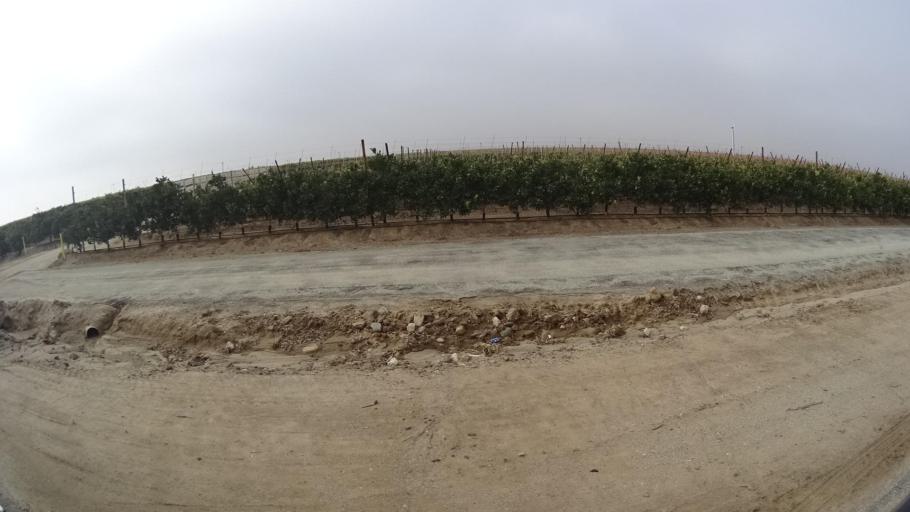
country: US
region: California
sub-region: Kern County
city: Maricopa
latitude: 35.0692
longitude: -119.3138
